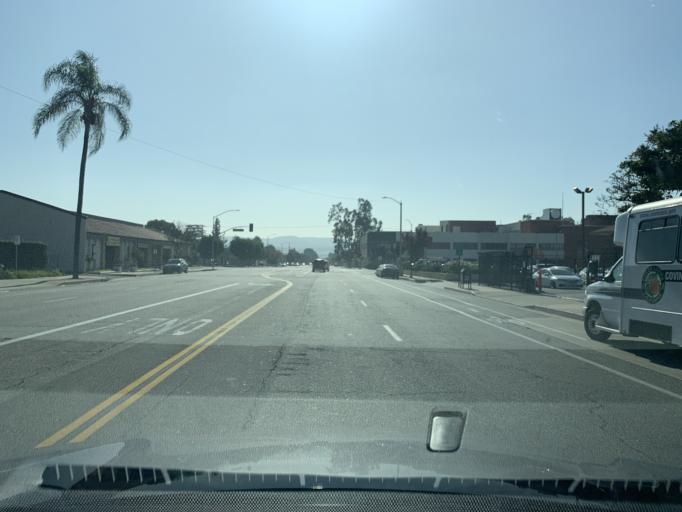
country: US
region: California
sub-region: Los Angeles County
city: Covina
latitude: 34.0873
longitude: -117.8880
